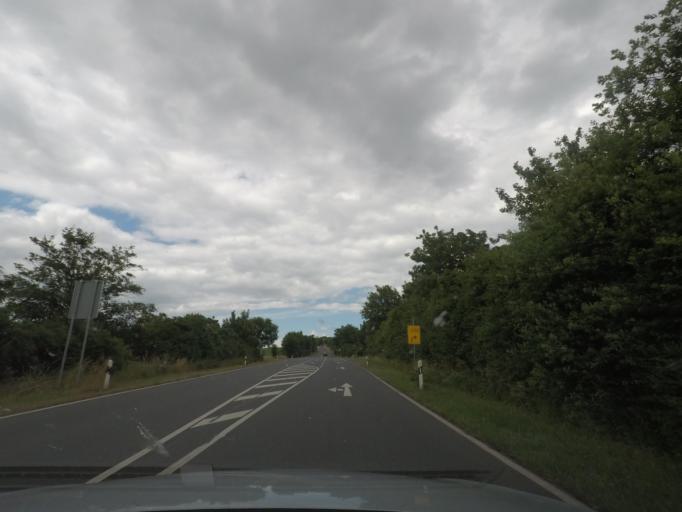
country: DE
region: Saxony-Anhalt
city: Volpke
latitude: 52.1032
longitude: 11.0770
